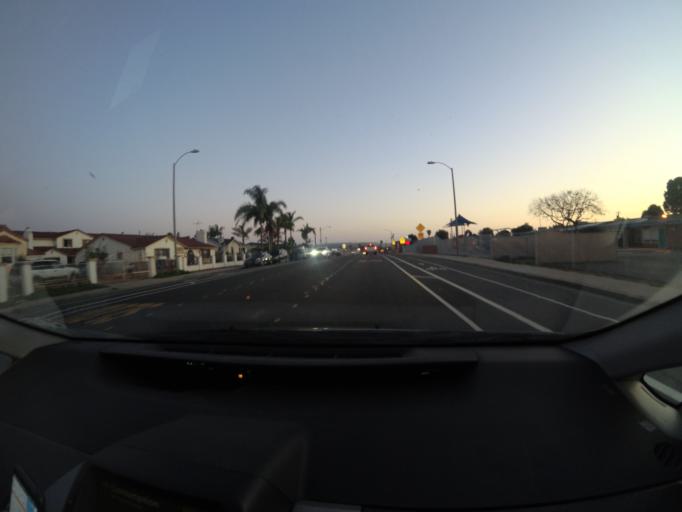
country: US
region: California
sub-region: San Diego County
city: Imperial Beach
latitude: 32.5787
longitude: -117.1057
